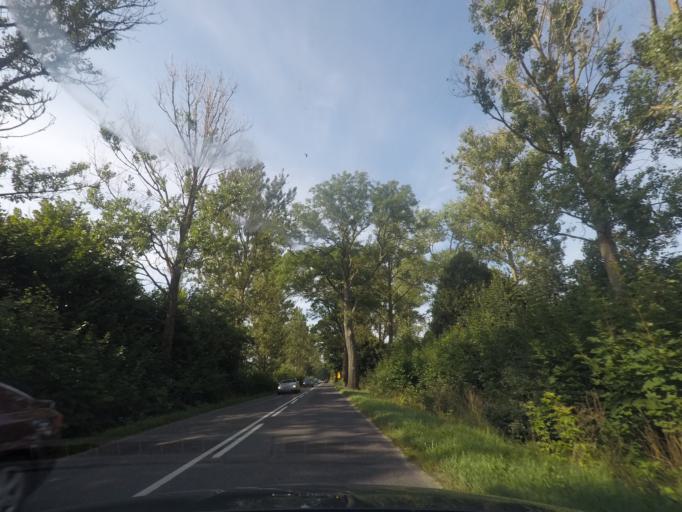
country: PL
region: Pomeranian Voivodeship
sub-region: Powiat leborski
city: Leba
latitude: 54.6844
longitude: 17.5959
